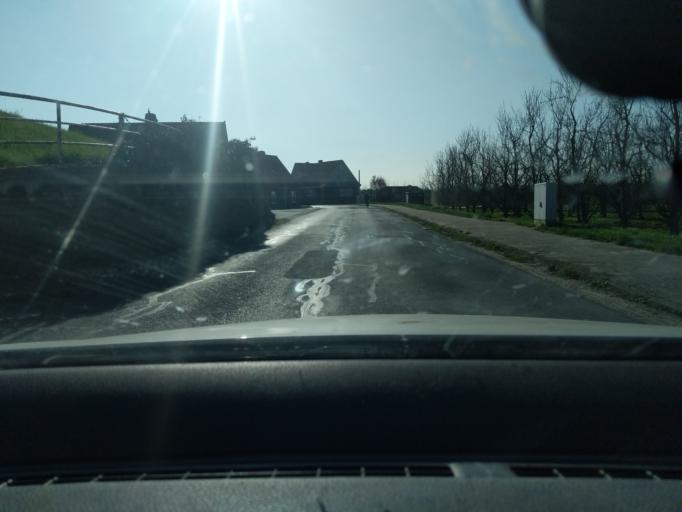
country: DE
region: Lower Saxony
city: Grunendeich
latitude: 53.5652
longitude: 9.6337
